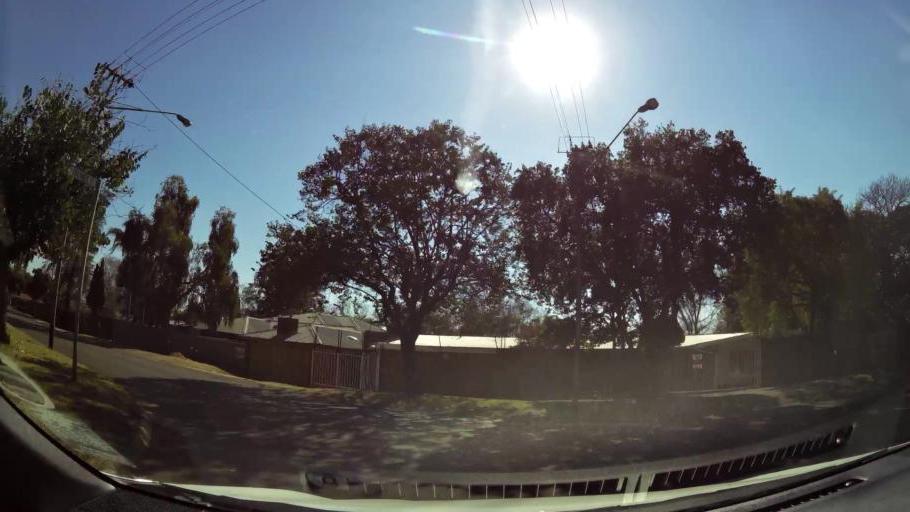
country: ZA
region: Gauteng
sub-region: City of Tshwane Metropolitan Municipality
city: Pretoria
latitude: -25.7762
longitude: 28.2144
